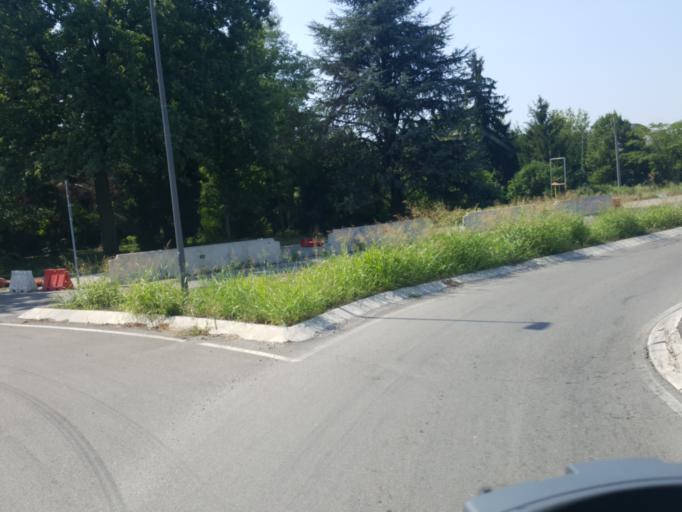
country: IT
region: Emilia-Romagna
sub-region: Provincia di Modena
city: San Vito
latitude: 44.5318
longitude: 10.9826
